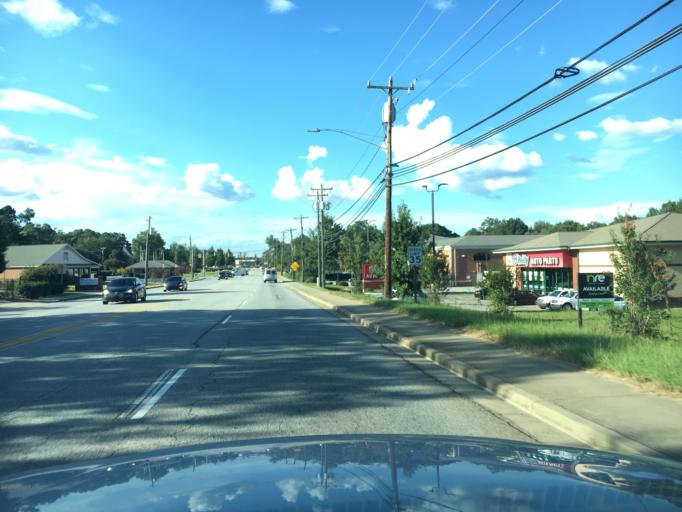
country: US
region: South Carolina
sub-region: Greenville County
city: Simpsonville
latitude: 34.7303
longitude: -82.2542
